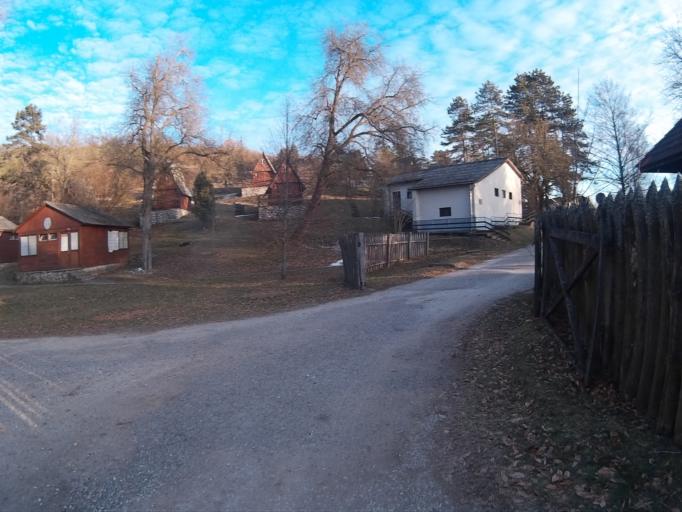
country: HU
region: Borsod-Abauj-Zemplen
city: Rudabanya
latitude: 48.4722
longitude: 20.4923
